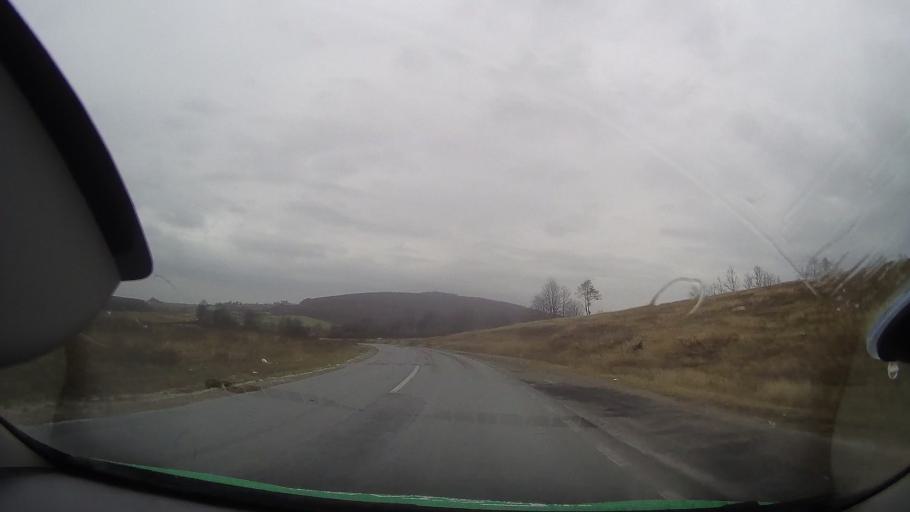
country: RO
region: Bihor
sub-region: Comuna Rabagani
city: Rabagani
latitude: 46.7277
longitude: 22.2399
